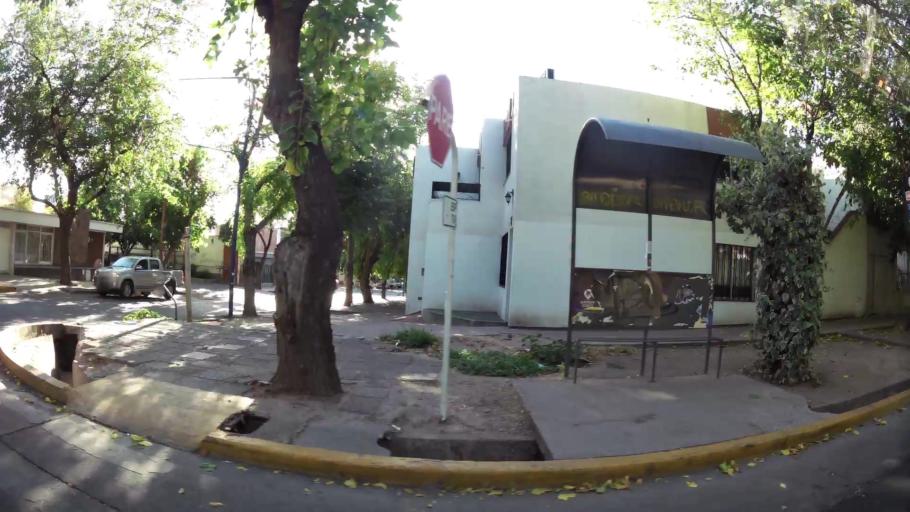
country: AR
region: Mendoza
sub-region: Departamento de Godoy Cruz
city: Godoy Cruz
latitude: -32.9154
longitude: -68.8504
